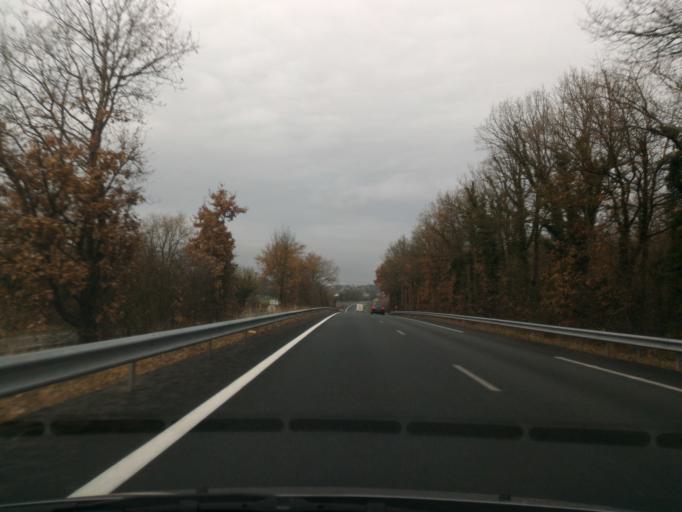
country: FR
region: Poitou-Charentes
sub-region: Departement de la Vienne
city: Iteuil
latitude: 46.4870
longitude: 0.2732
